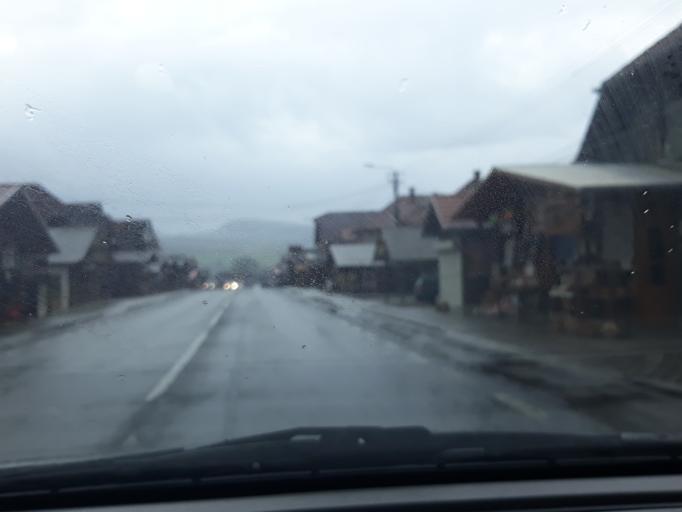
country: RO
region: Harghita
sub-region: Comuna Corund
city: Corund
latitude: 46.4732
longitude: 25.1814
